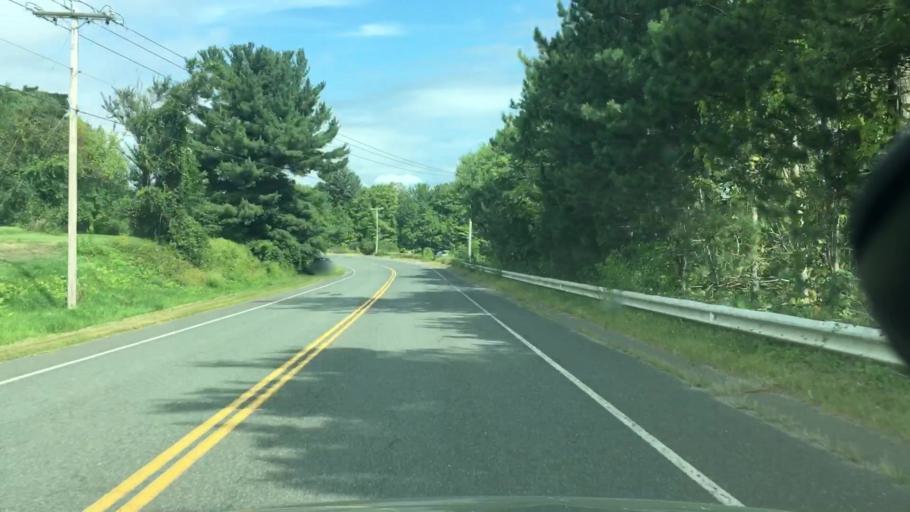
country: US
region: Massachusetts
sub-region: Franklin County
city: Colrain
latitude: 42.6543
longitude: -72.6769
